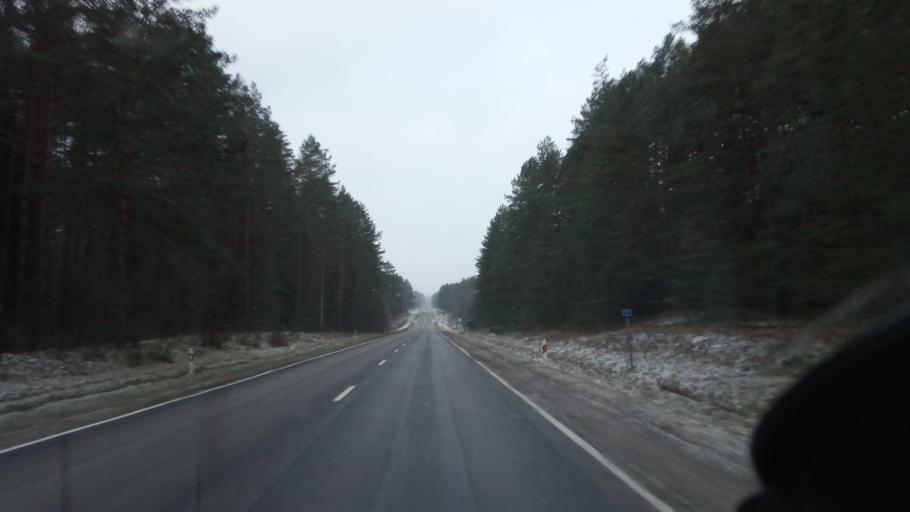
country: LT
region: Vilnius County
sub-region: Trakai
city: Rudiskes
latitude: 54.3535
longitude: 24.7872
